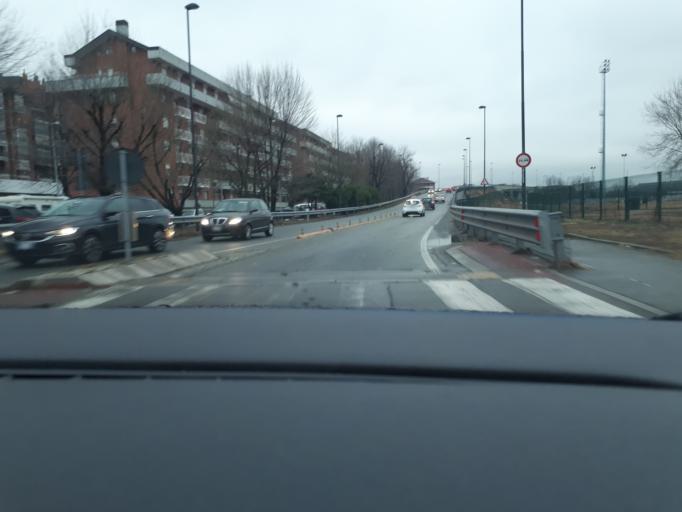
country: IT
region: Piedmont
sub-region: Provincia di Torino
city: Lesna
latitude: 45.0671
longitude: 7.6081
